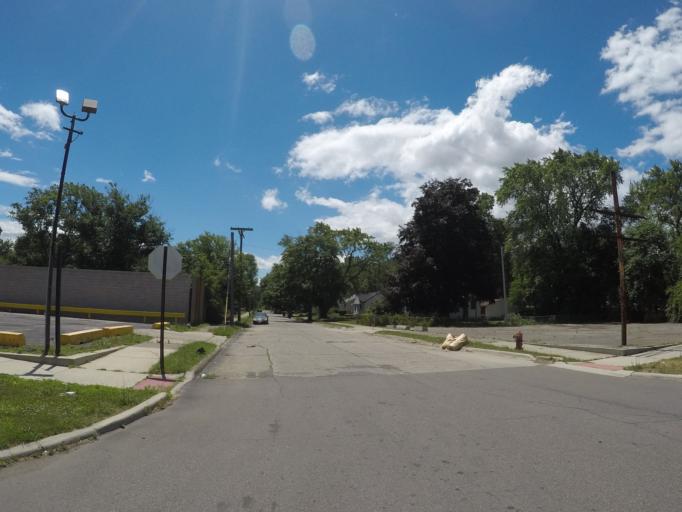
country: US
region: Michigan
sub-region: Oakland County
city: Southfield
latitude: 42.4292
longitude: -83.2520
